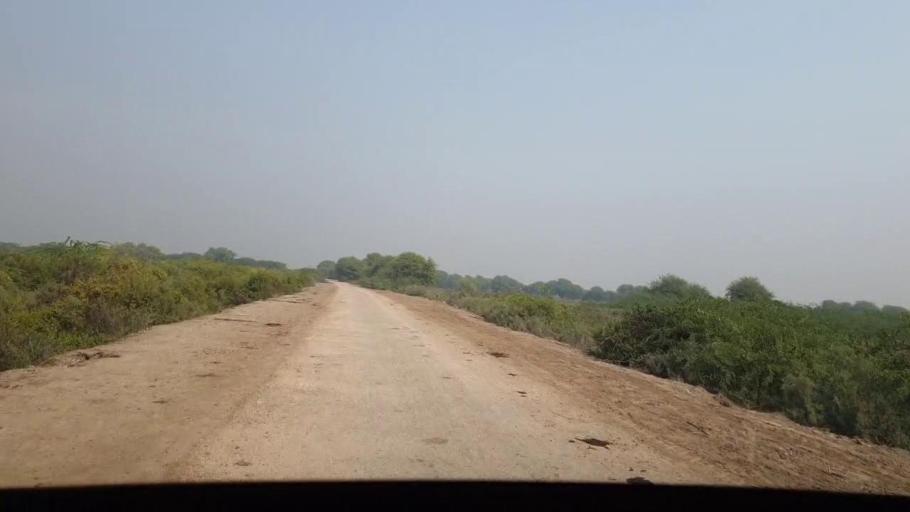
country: PK
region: Sindh
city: Jati
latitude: 24.4314
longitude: 68.4337
